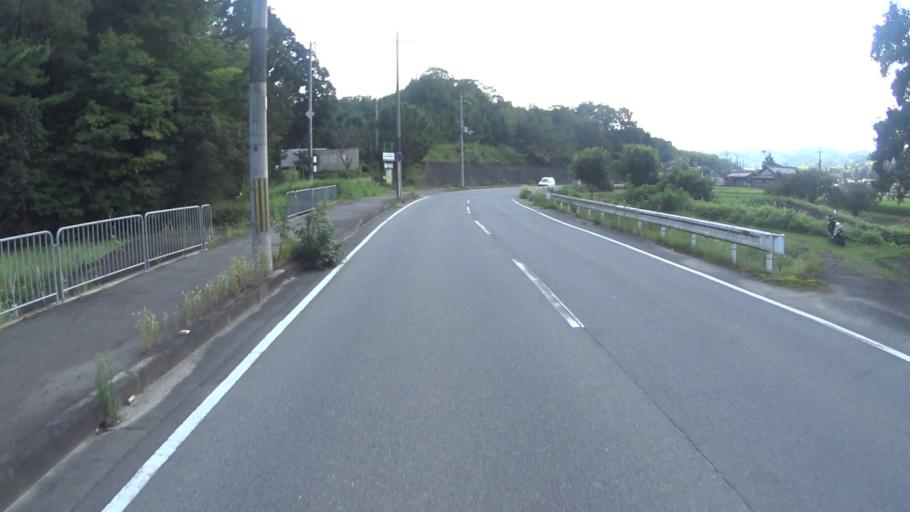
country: JP
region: Kyoto
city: Tanabe
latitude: 34.7913
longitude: 135.7601
